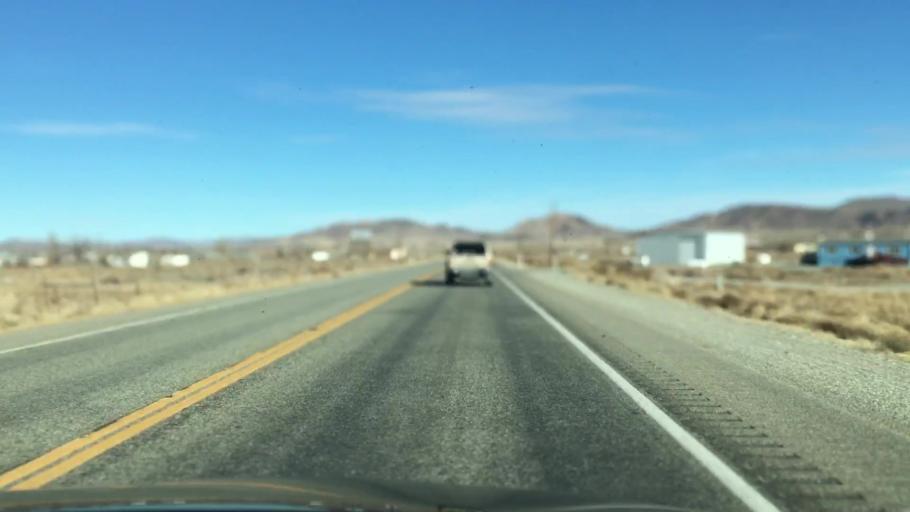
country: US
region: Nevada
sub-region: Lyon County
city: Yerington
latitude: 39.0105
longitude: -119.0774
